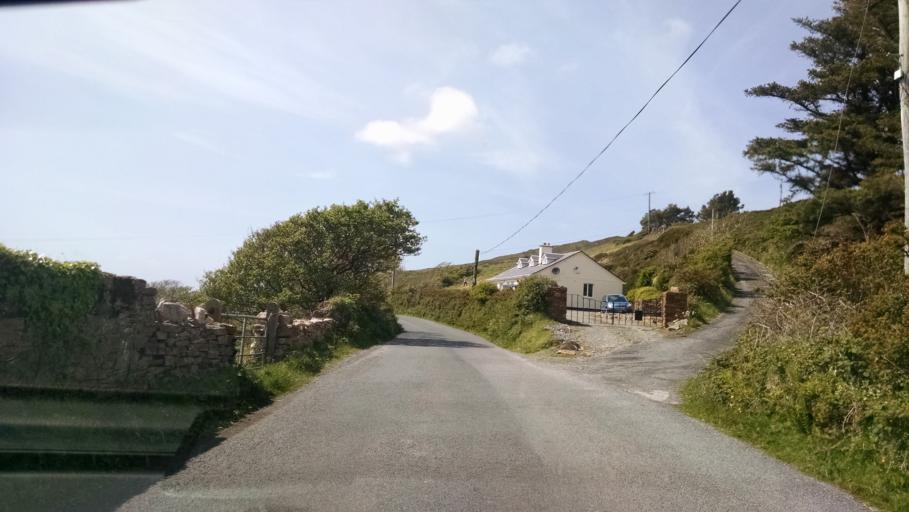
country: IE
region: Connaught
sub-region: County Galway
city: Clifden
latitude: 53.4938
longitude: -10.0554
